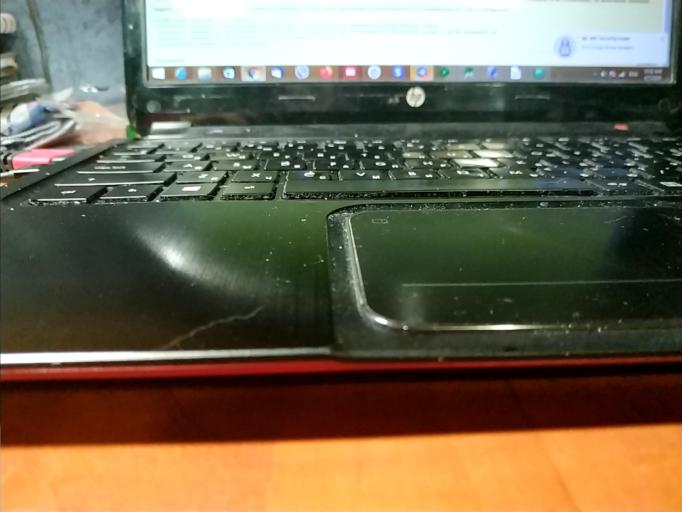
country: RU
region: Vologda
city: Suda
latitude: 58.9137
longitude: 37.5432
